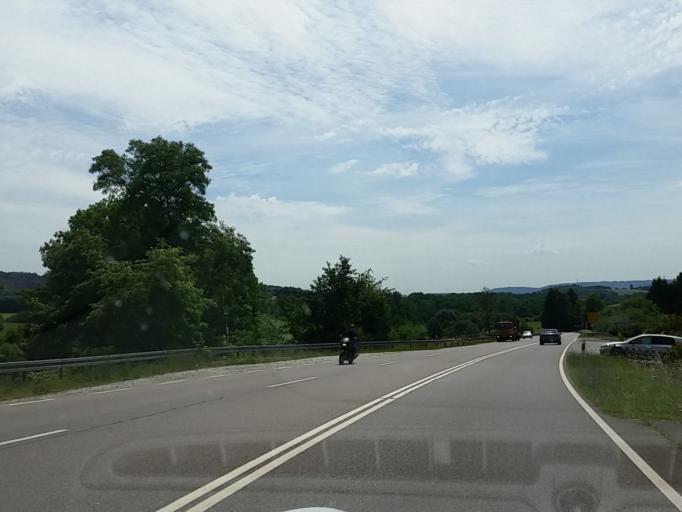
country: DE
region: Saarland
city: Schmelz
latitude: 49.4710
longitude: 6.8394
